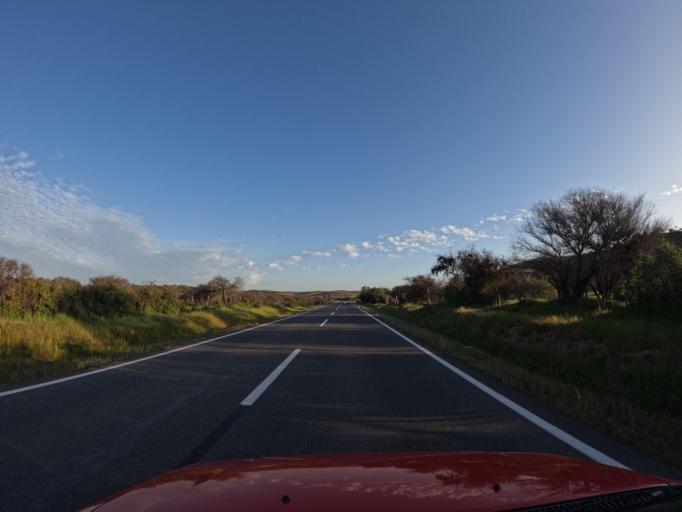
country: CL
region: O'Higgins
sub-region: Provincia de Colchagua
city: Santa Cruz
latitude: -34.2835
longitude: -71.7294
